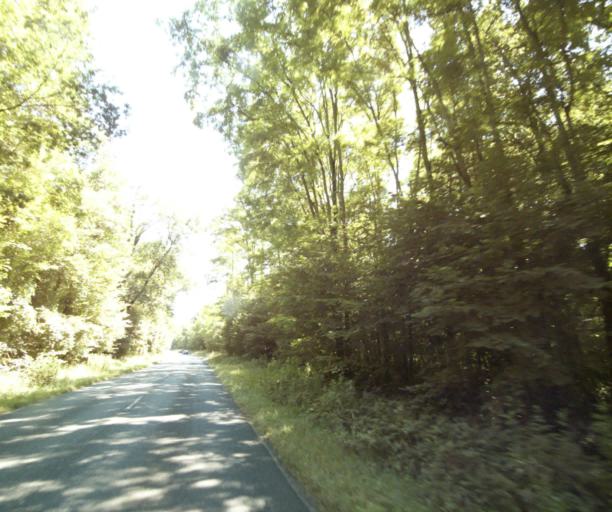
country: FR
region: Ile-de-France
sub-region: Departement de Seine-et-Marne
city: Noisy-sur-Ecole
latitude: 48.3741
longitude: 2.5053
